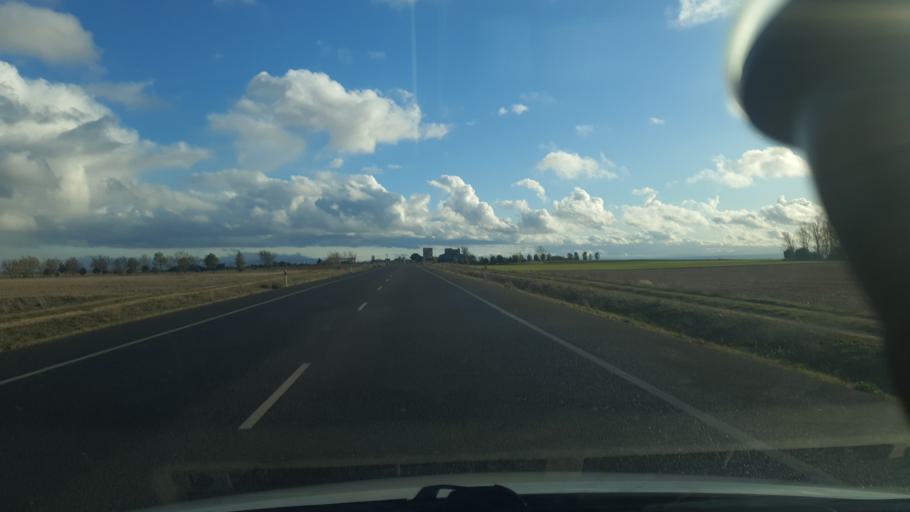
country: ES
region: Castille and Leon
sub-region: Provincia de Segovia
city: Codorniz
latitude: 41.0609
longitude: -4.6311
